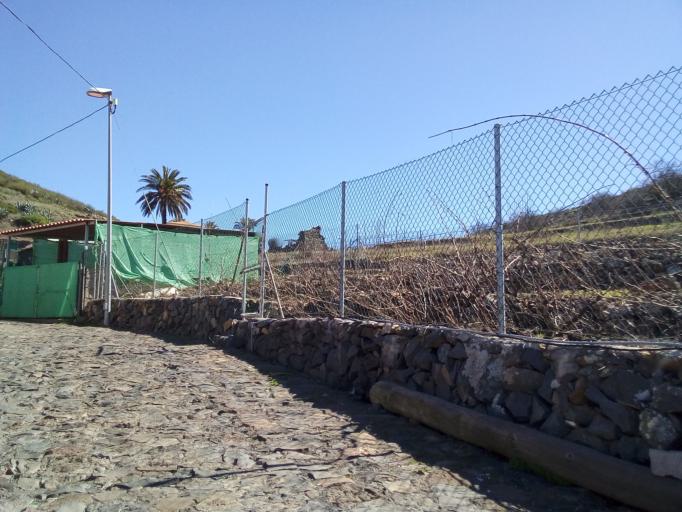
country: ES
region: Canary Islands
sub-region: Provincia de Santa Cruz de Tenerife
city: Alajero
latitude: 28.1034
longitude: -17.2749
